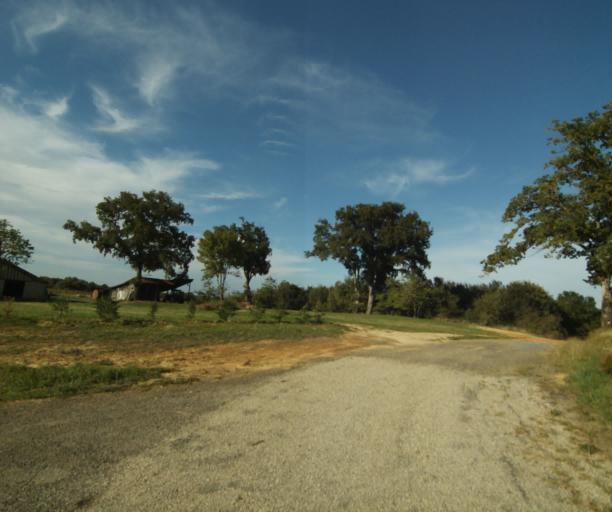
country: FR
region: Midi-Pyrenees
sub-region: Departement du Gers
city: Eauze
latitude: 43.8650
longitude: 0.0563
